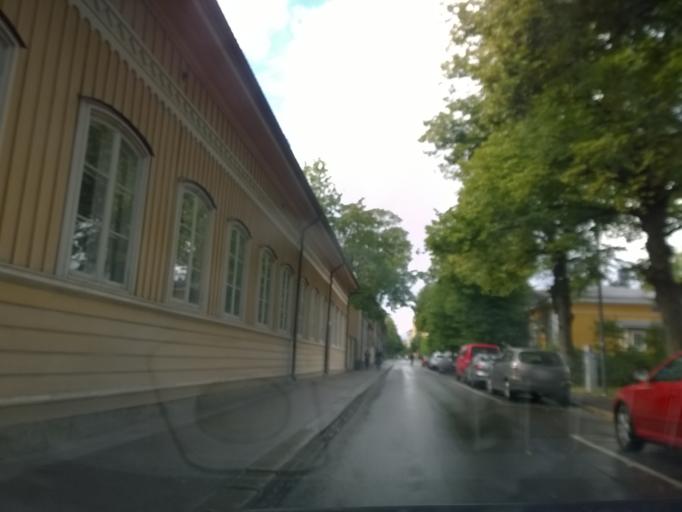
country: FI
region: Pirkanmaa
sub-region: Tampere
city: Tampere
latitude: 61.5017
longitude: 23.7543
